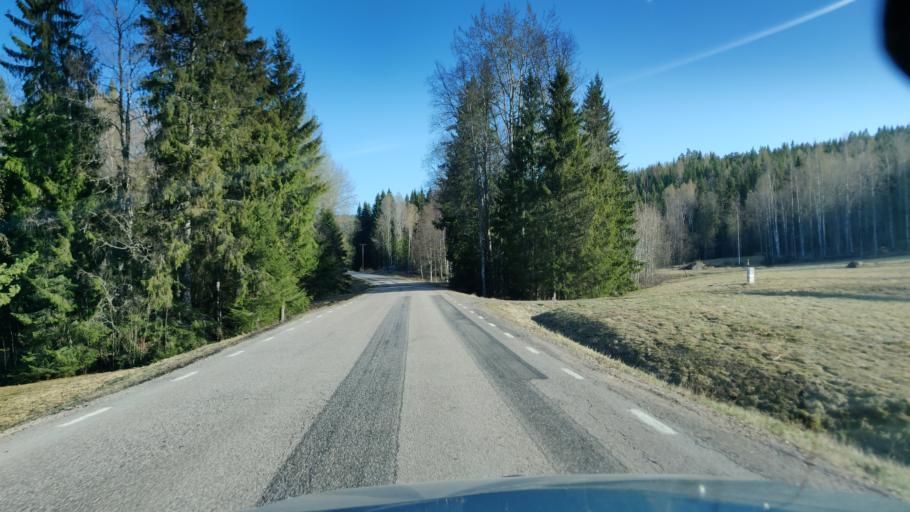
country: SE
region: Vaermland
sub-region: Munkfors Kommun
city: Munkfors
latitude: 59.9748
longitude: 13.4141
